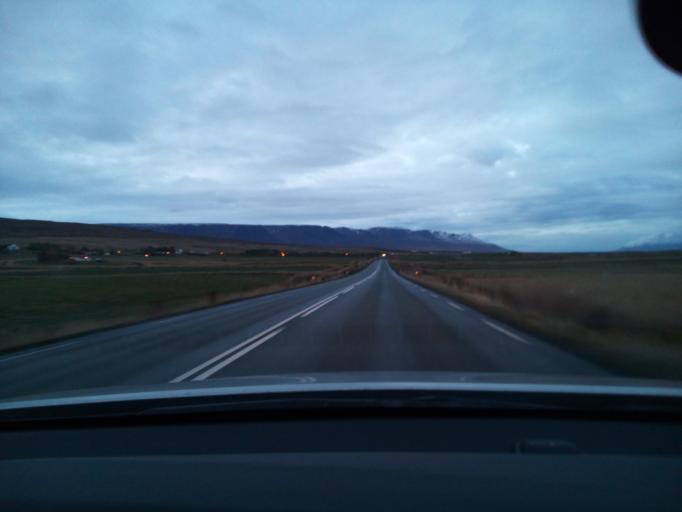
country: IS
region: Northeast
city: Akureyri
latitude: 65.7139
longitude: -18.1674
